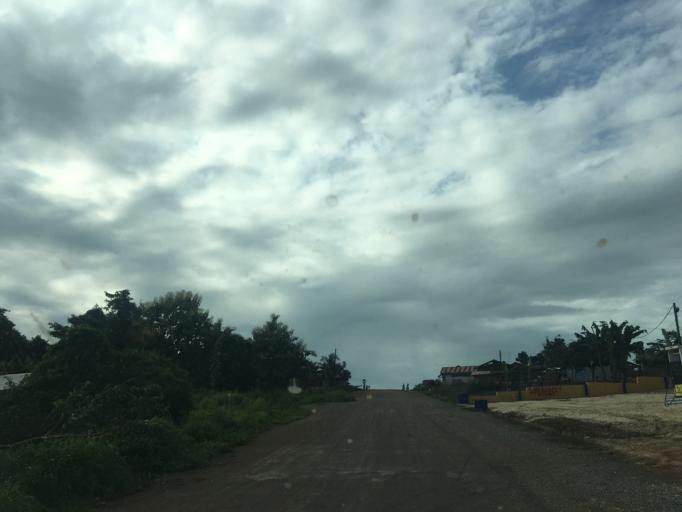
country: GH
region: Western
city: Wassa-Akropong
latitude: 5.9967
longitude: -2.4102
